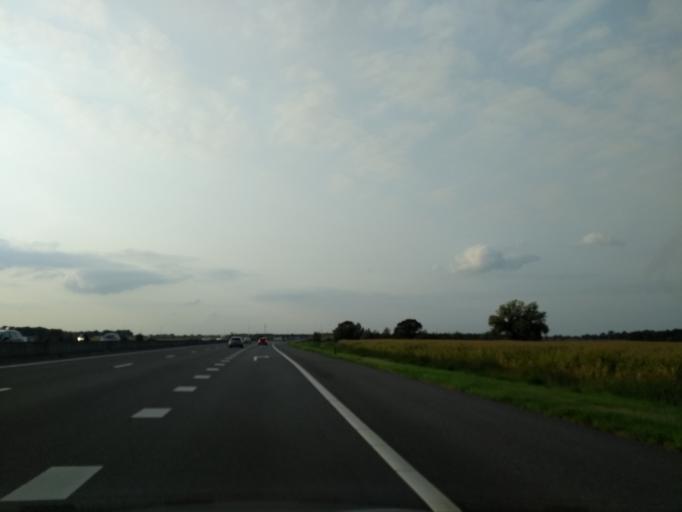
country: NL
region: Overijssel
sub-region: Gemeente Wierden
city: Wierden
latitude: 52.3377
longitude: 6.6010
